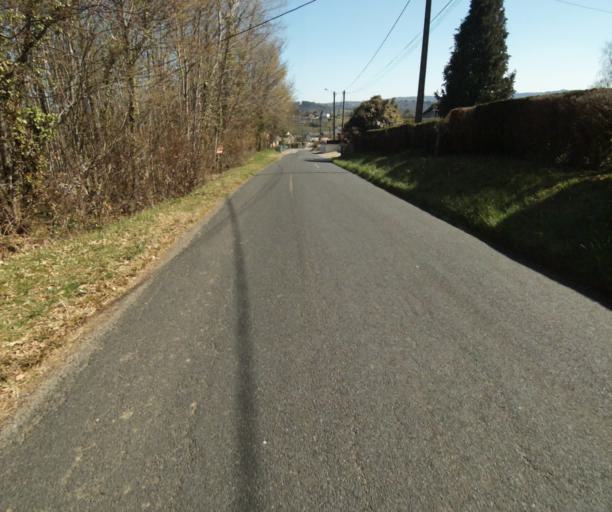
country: FR
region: Limousin
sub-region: Departement de la Correze
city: Tulle
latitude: 45.2601
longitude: 1.7389
